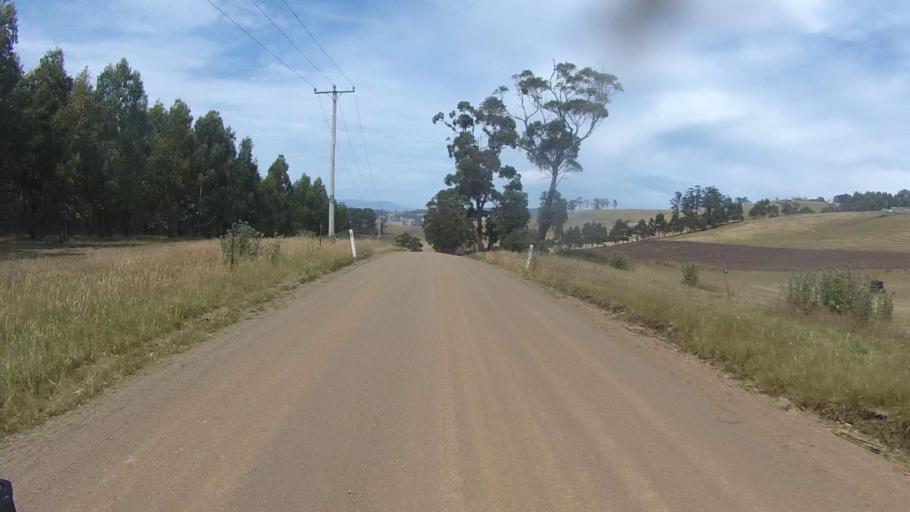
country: AU
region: Tasmania
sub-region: Sorell
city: Sorell
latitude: -42.7821
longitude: 147.8434
